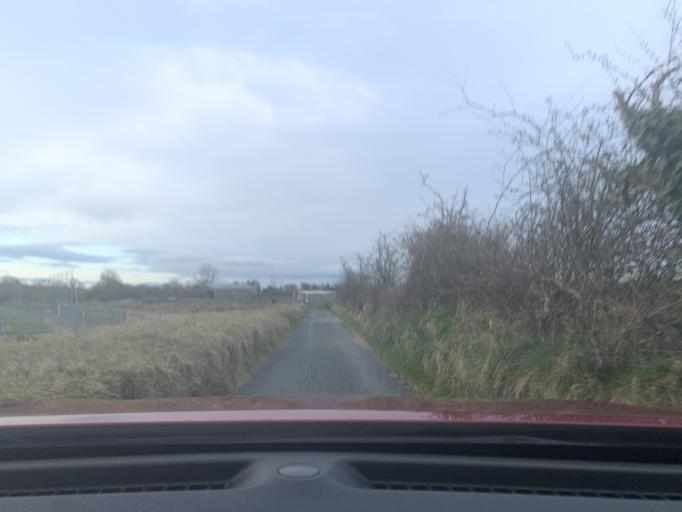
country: IE
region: Connaught
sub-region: Roscommon
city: Ballaghaderreen
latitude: 53.8974
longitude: -8.5903
